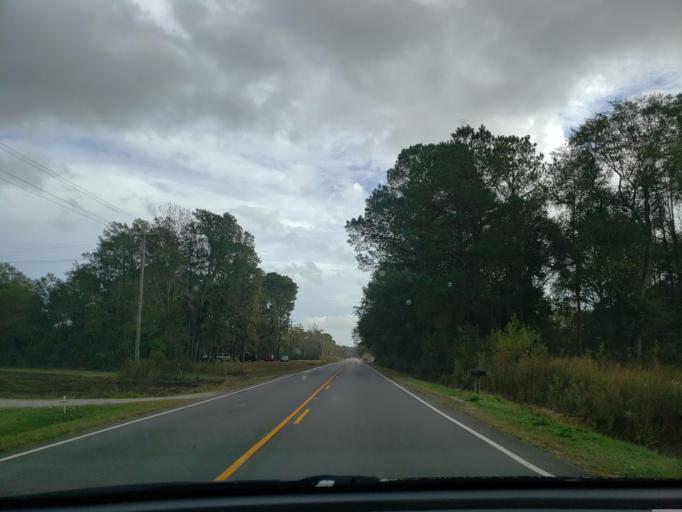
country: US
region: North Carolina
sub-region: Duplin County
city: Beulaville
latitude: 34.8386
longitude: -77.8623
